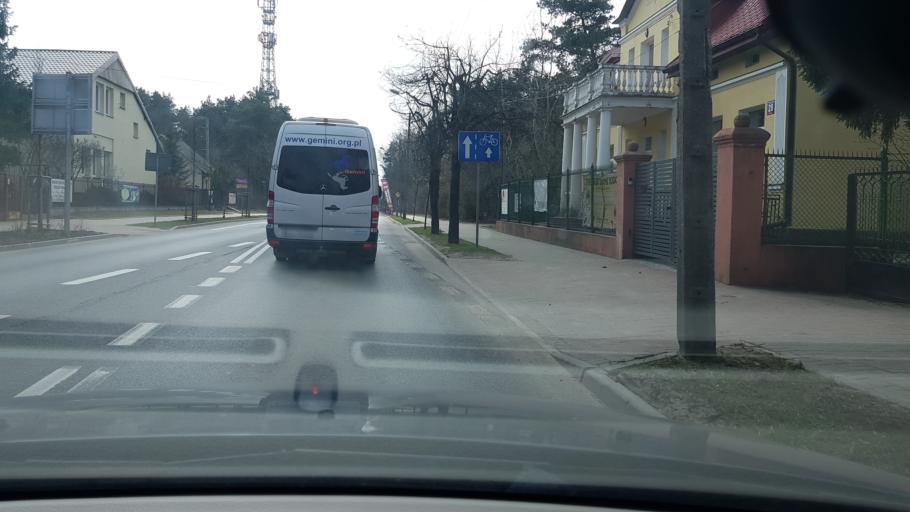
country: PL
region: Masovian Voivodeship
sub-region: Warszawa
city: Wesola
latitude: 52.2504
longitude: 21.2237
